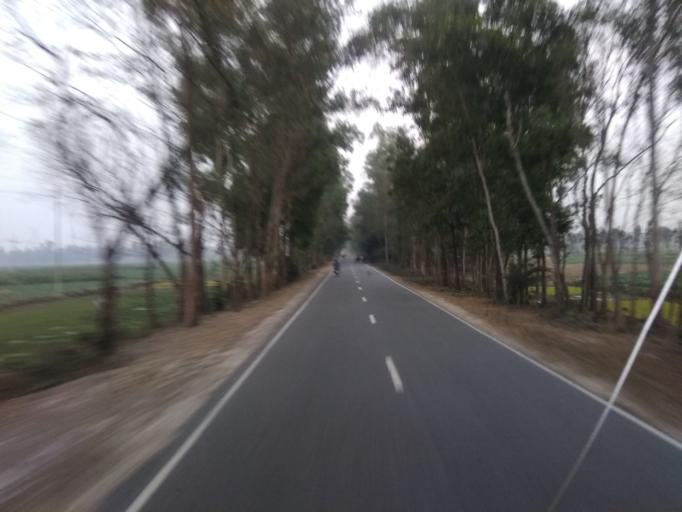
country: BD
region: Rajshahi
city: Bogra
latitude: 24.6730
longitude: 89.2799
